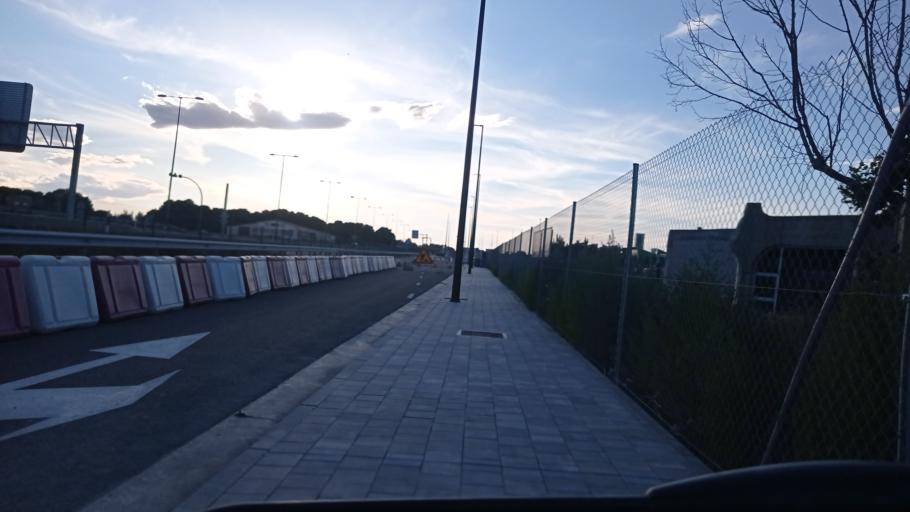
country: ES
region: Aragon
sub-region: Provincia de Zaragoza
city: Oliver-Valdefierro, Oliver, Valdefierro
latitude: 41.6741
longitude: -0.9524
